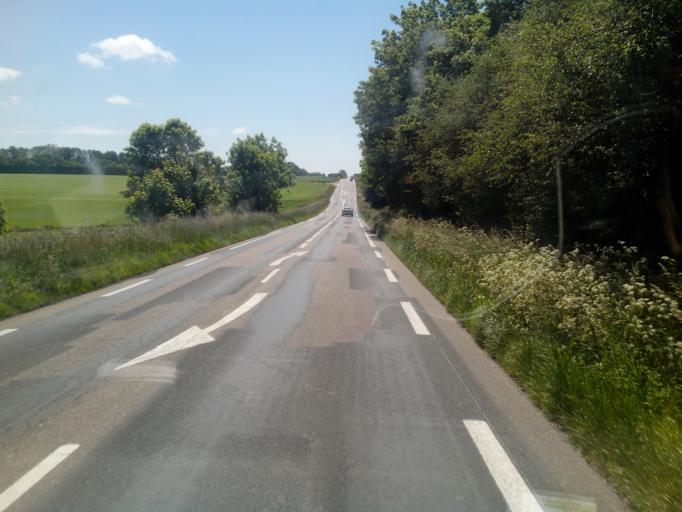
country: FR
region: Haute-Normandie
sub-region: Departement de la Seine-Maritime
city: Turretot
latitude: 49.6069
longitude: 0.2829
